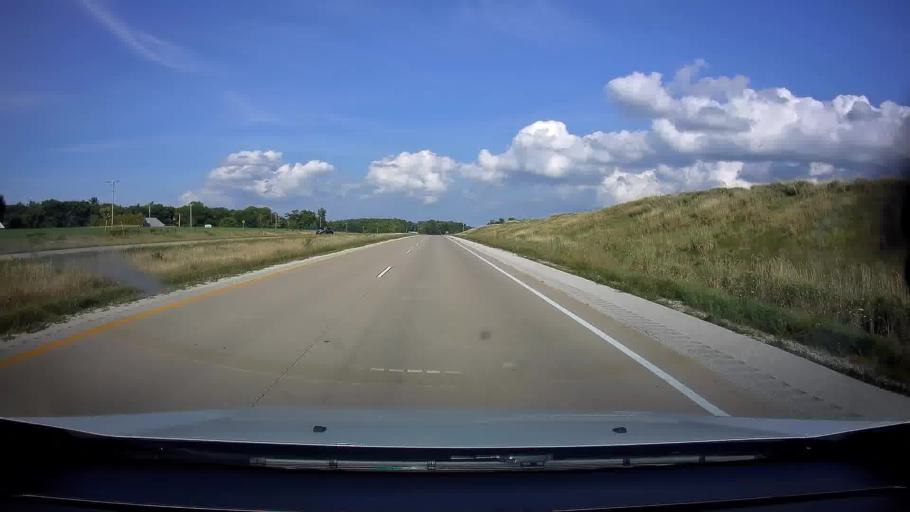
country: US
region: Wisconsin
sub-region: Kewaunee County
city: Luxemburg
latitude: 44.7136
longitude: -87.6854
